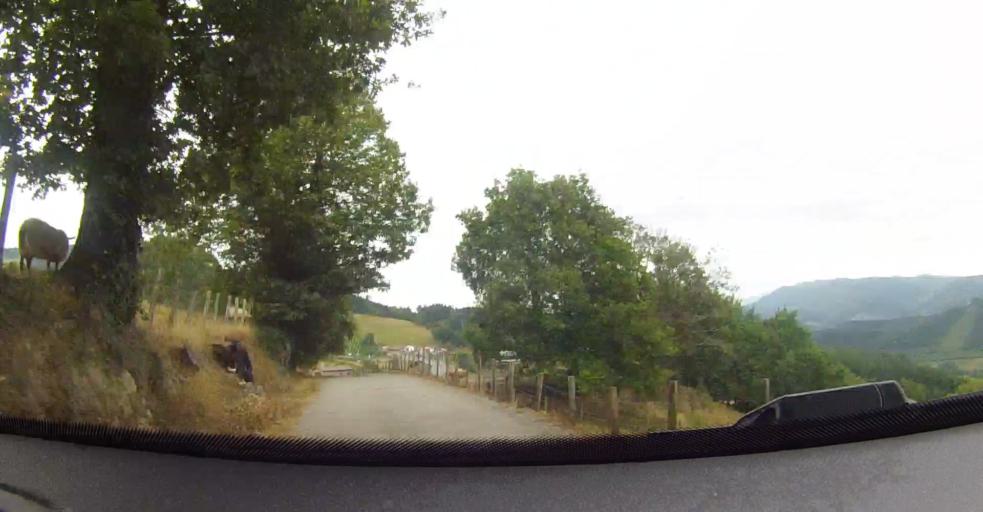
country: ES
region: Basque Country
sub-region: Bizkaia
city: Urrestieta
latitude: 43.2290
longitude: -3.1656
